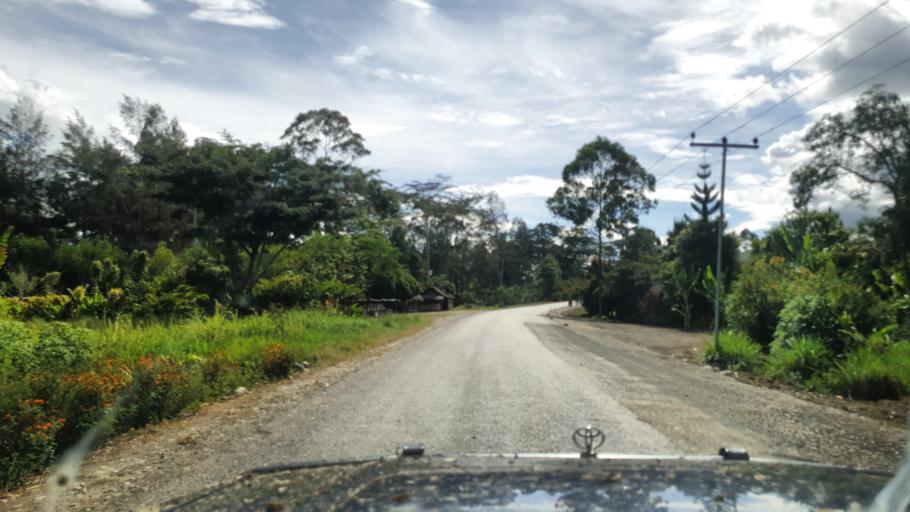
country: PG
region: Jiwaka
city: Minj
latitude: -5.8844
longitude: 144.7257
